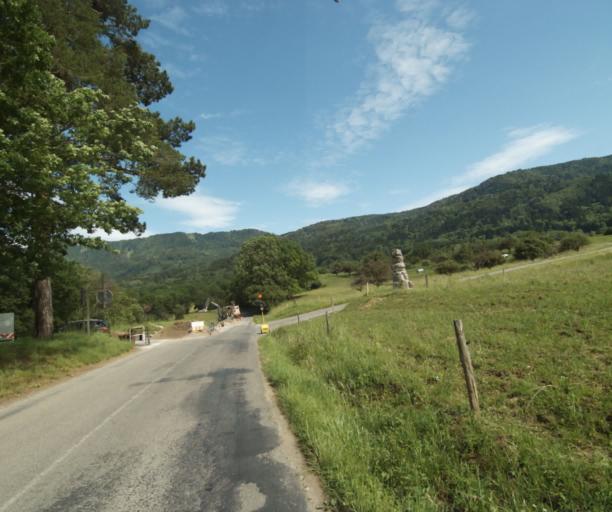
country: FR
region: Rhone-Alpes
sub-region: Departement de la Haute-Savoie
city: Bons-en-Chablais
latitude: 46.2785
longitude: 6.4171
